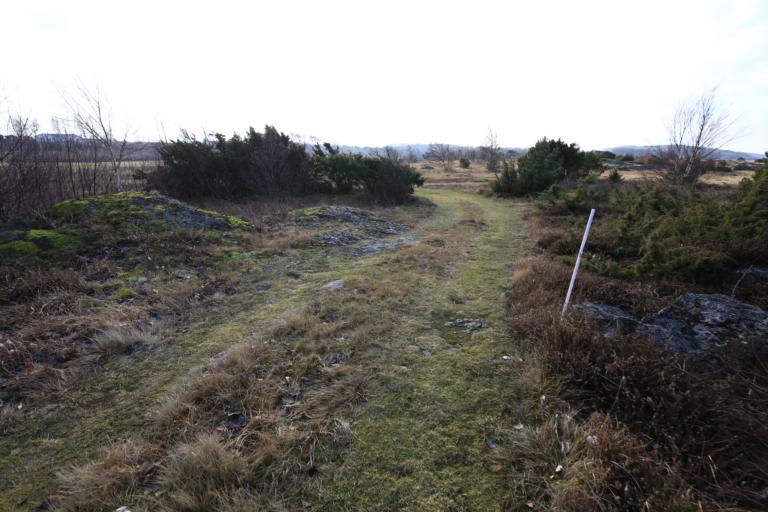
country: SE
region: Halland
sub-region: Varbergs Kommun
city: Varberg
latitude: 57.2117
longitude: 12.2140
